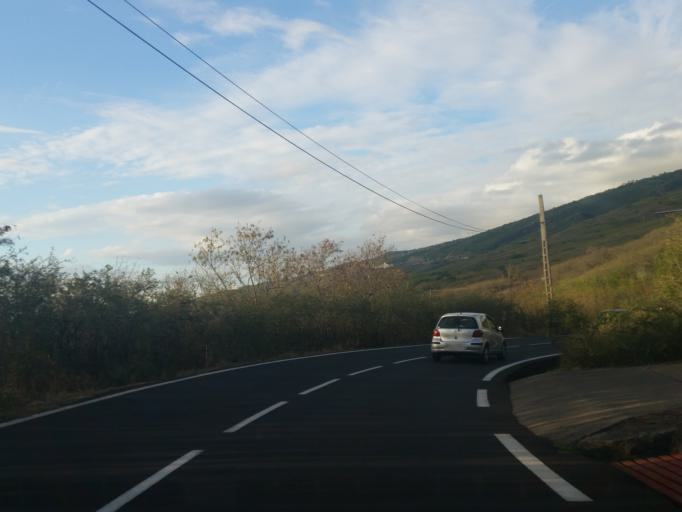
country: RE
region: Reunion
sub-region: Reunion
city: Saint-Leu
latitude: -21.1373
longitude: 55.2811
